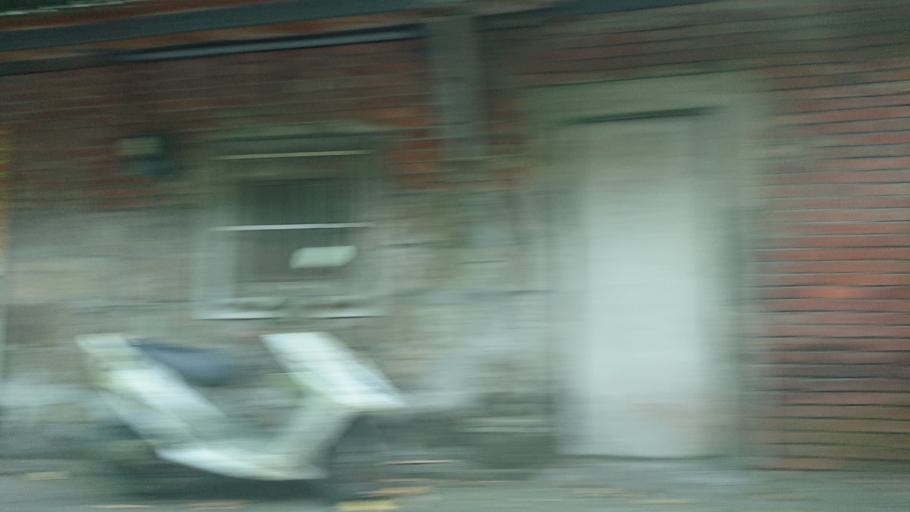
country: TW
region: Taiwan
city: Daxi
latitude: 24.8815
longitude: 121.3798
